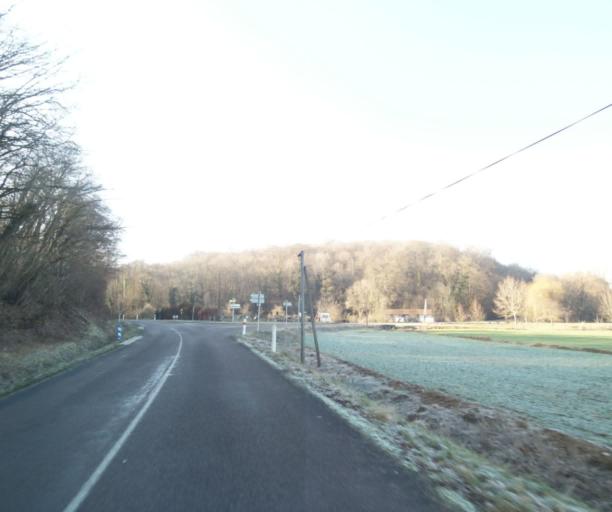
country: FR
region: Champagne-Ardenne
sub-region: Departement de la Haute-Marne
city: Bienville
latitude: 48.5549
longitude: 5.0881
